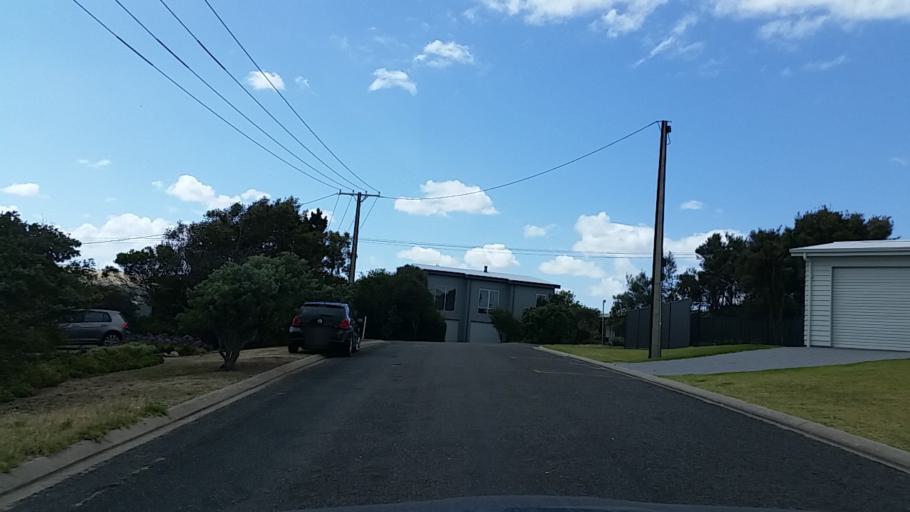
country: AU
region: South Australia
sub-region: Alexandrina
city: Port Elliot
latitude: -35.5343
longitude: 138.6729
